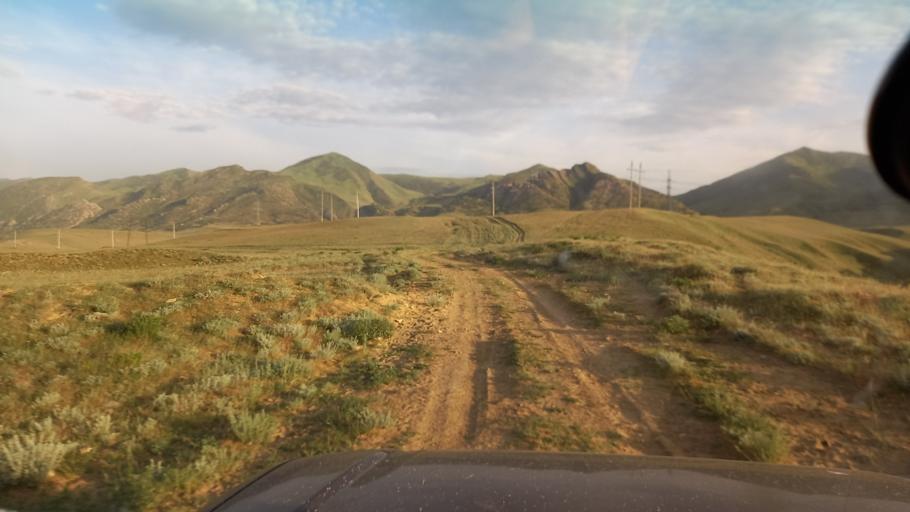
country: RU
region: Dagestan
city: Korkmaskala
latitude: 42.9934
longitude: 47.2450
